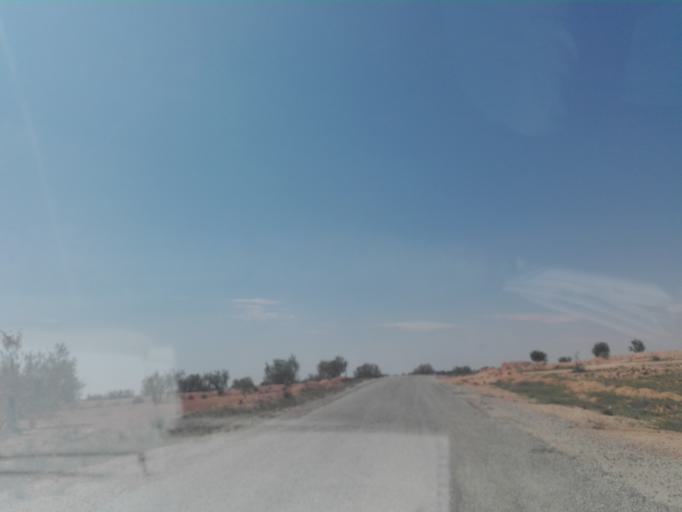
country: TN
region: Safaqis
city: Bi'r `Ali Bin Khalifah
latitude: 34.6420
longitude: 10.4083
